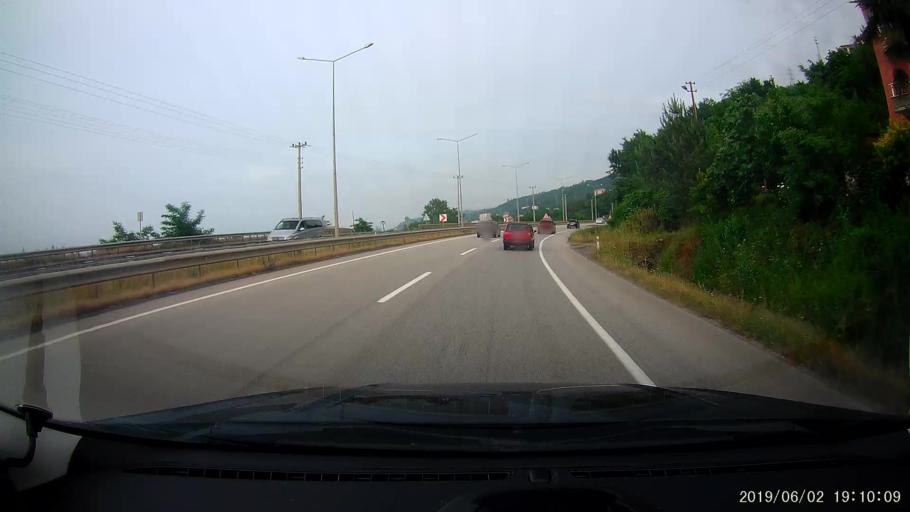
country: TR
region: Ordu
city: Gulyali
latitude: 40.9710
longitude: 38.0403
